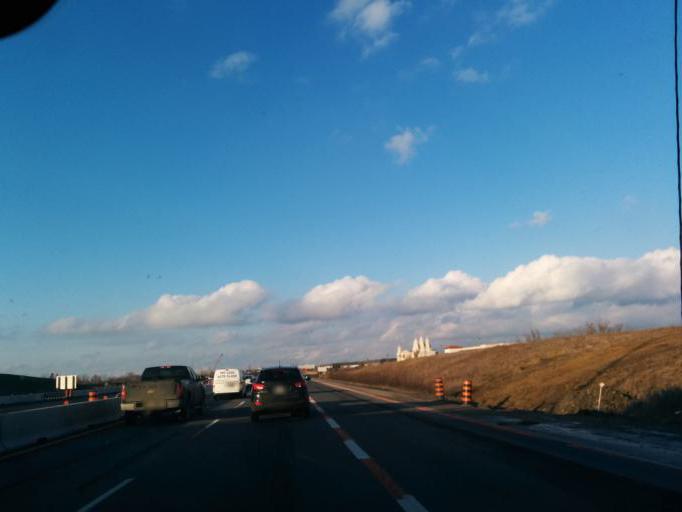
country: CA
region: Ontario
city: Etobicoke
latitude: 43.7344
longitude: -79.6271
